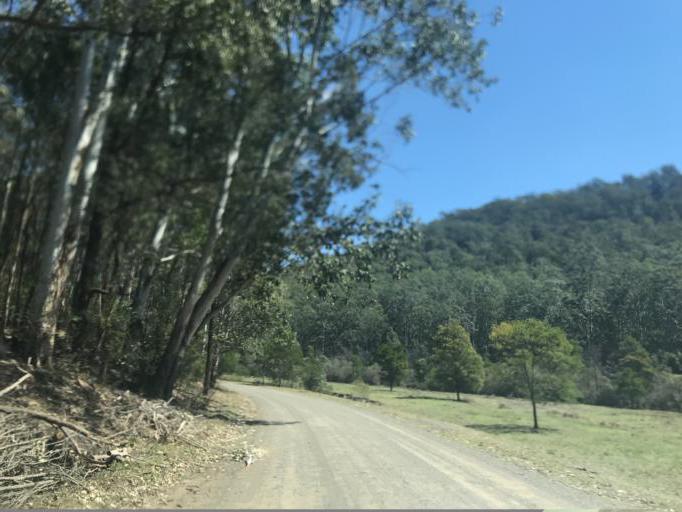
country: AU
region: New South Wales
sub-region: Wyong Shire
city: Little Jilliby
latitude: -33.2032
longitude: 150.9882
